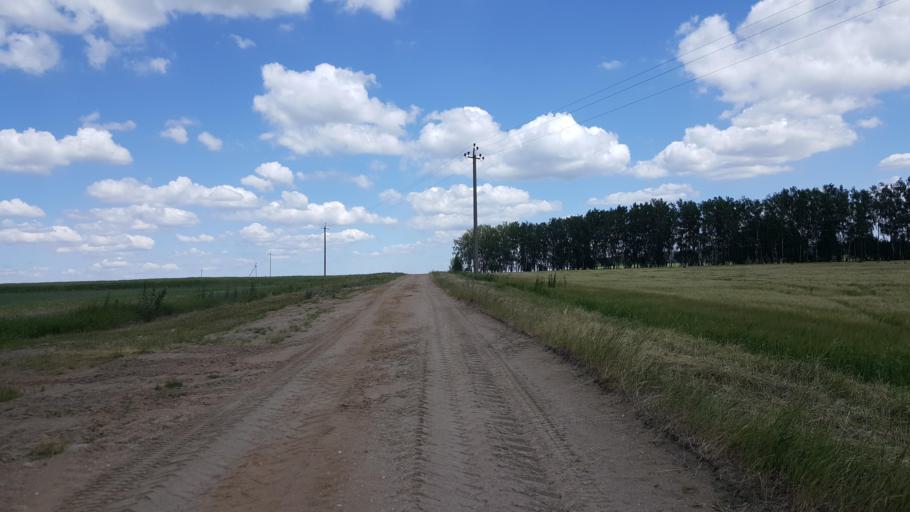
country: BY
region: Brest
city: Vysokaye
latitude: 52.4177
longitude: 23.5251
